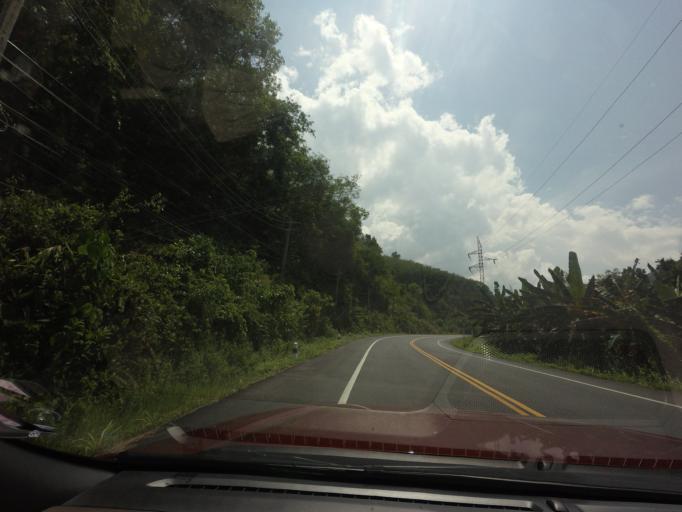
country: TH
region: Yala
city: Than To
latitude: 5.9773
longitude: 101.2004
